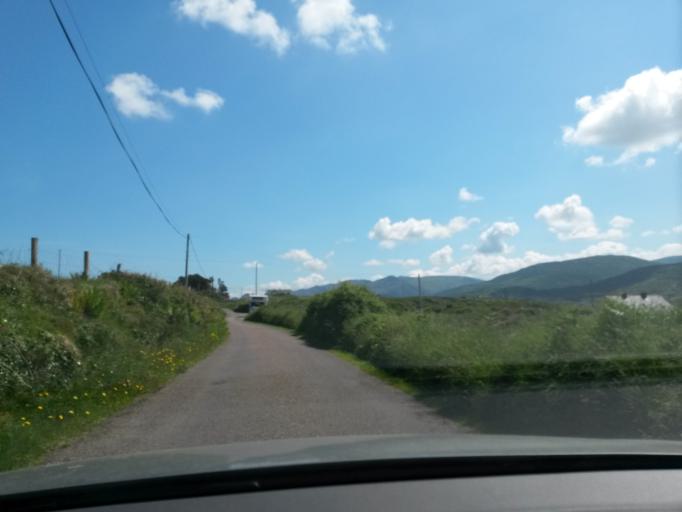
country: IE
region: Munster
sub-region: Ciarrai
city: Cahersiveen
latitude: 51.7158
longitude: -9.9674
